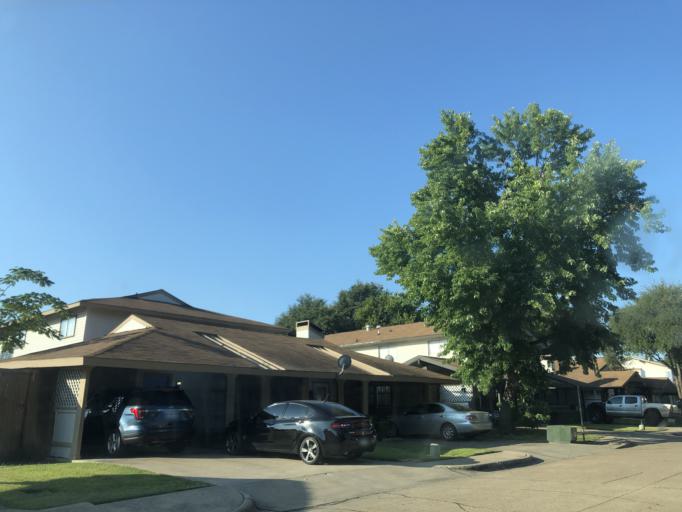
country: US
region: Texas
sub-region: Dallas County
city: Garland
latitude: 32.8604
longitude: -96.6396
